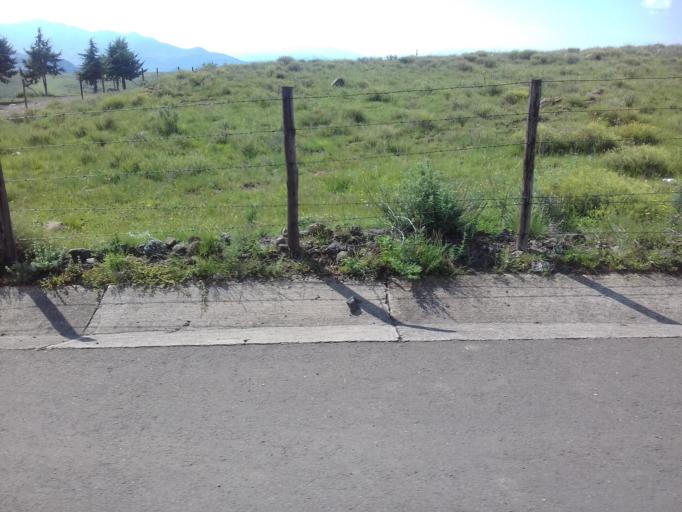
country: LS
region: Thaba-Tseka
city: Thaba-Tseka
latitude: -29.5180
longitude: 28.6189
